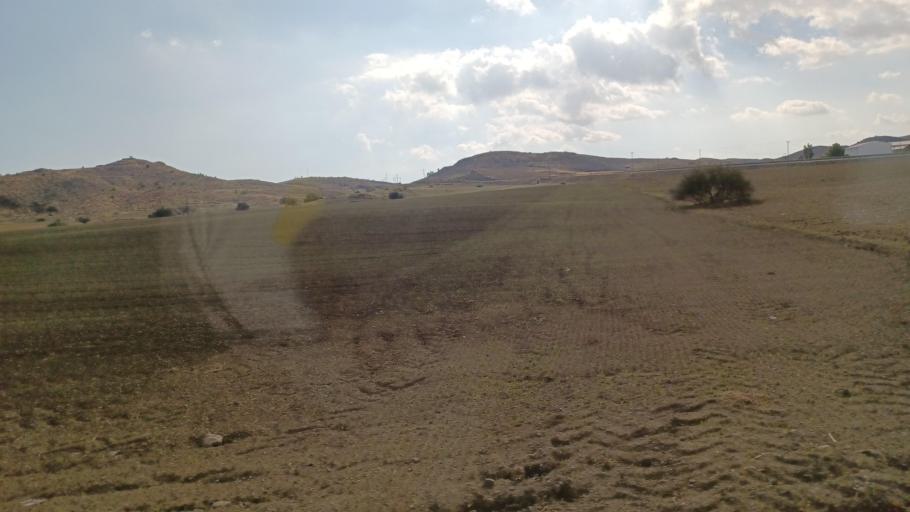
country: CY
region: Larnaka
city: Troulloi
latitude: 35.0145
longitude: 33.6242
